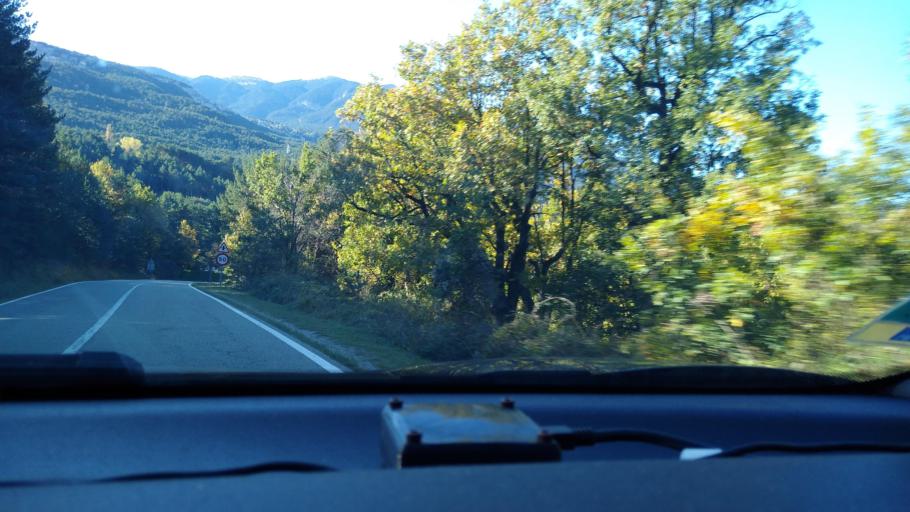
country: ES
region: Catalonia
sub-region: Provincia de Barcelona
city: Saldes
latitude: 42.2298
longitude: 1.7603
